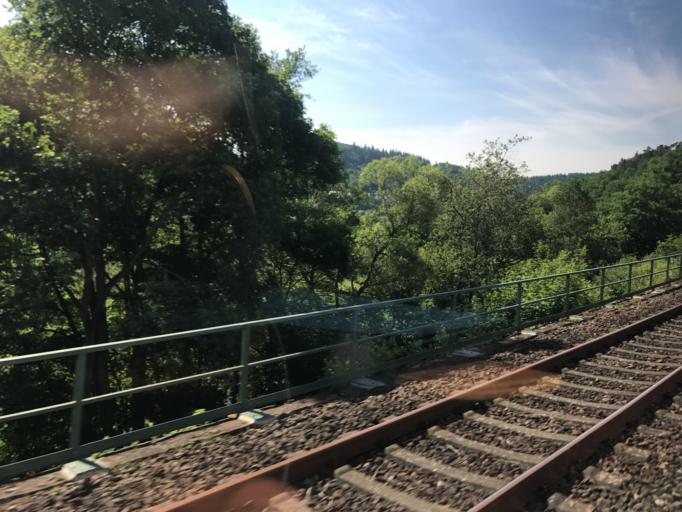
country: DE
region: Rheinland-Pfalz
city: Frauenberg
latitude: 49.6781
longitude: 7.2845
